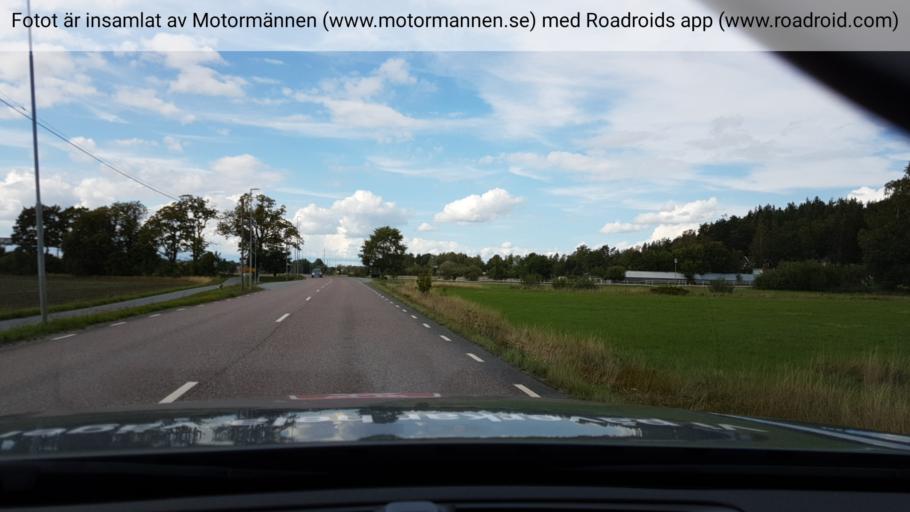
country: SE
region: Stockholm
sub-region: Upplands-Bro Kommun
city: Bro
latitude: 59.4998
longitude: 17.6710
